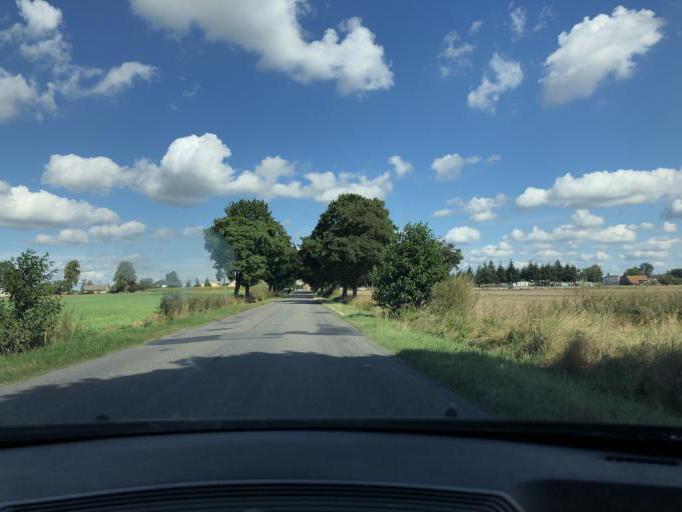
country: PL
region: Lodz Voivodeship
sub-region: Powiat wieruszowski
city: Czastary
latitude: 51.2527
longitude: 18.3171
